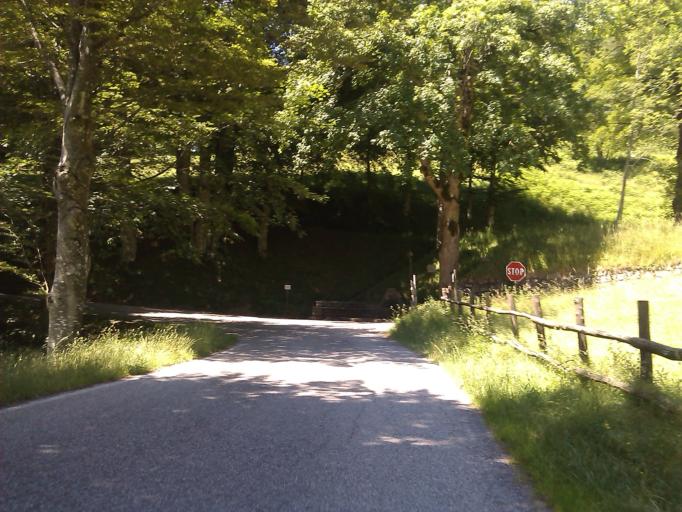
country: IT
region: Tuscany
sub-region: Provincia di Prato
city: Cantagallo
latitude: 44.0087
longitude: 11.0163
